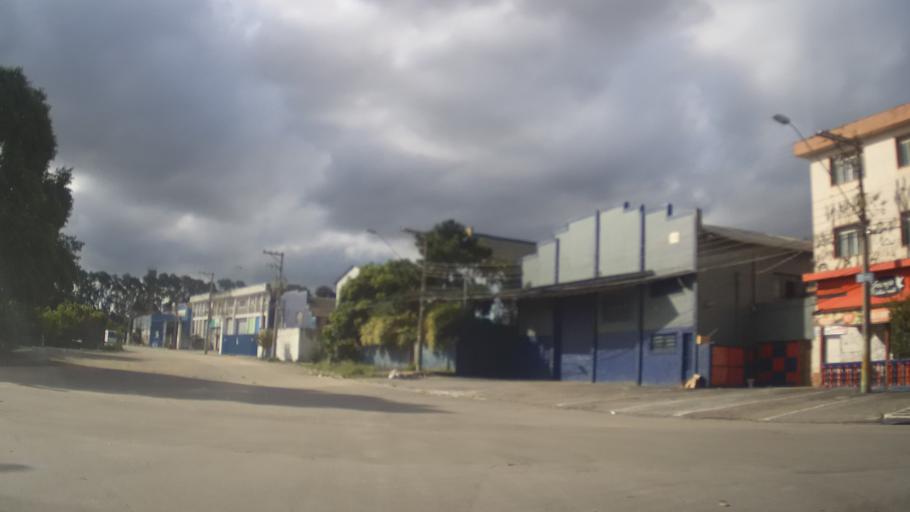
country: BR
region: Sao Paulo
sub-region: Guarulhos
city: Guarulhos
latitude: -23.4644
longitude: -46.4757
